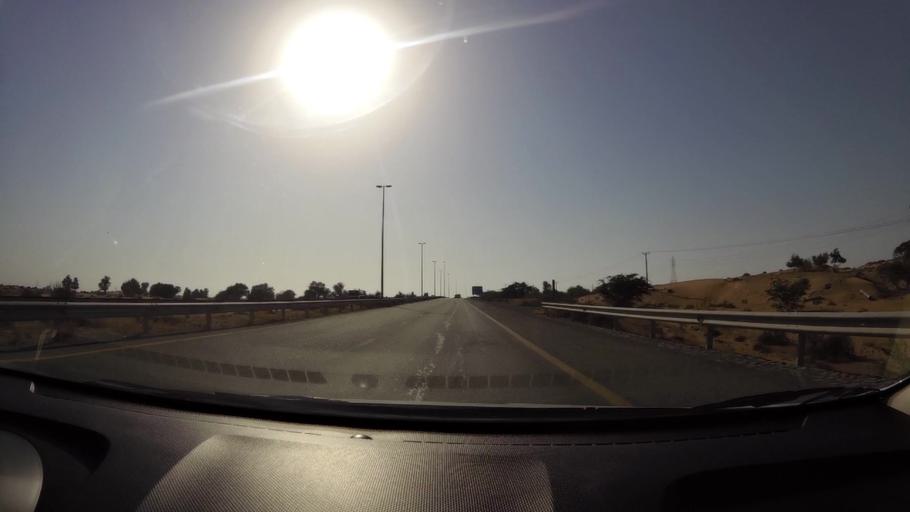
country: AE
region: Umm al Qaywayn
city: Umm al Qaywayn
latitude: 25.4457
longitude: 55.6243
